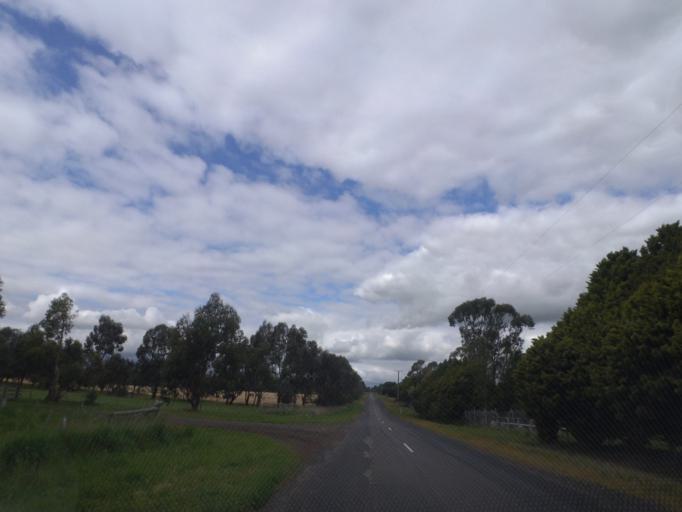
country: AU
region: Victoria
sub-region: Hume
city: Craigieburn
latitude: -37.4647
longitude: 144.9336
